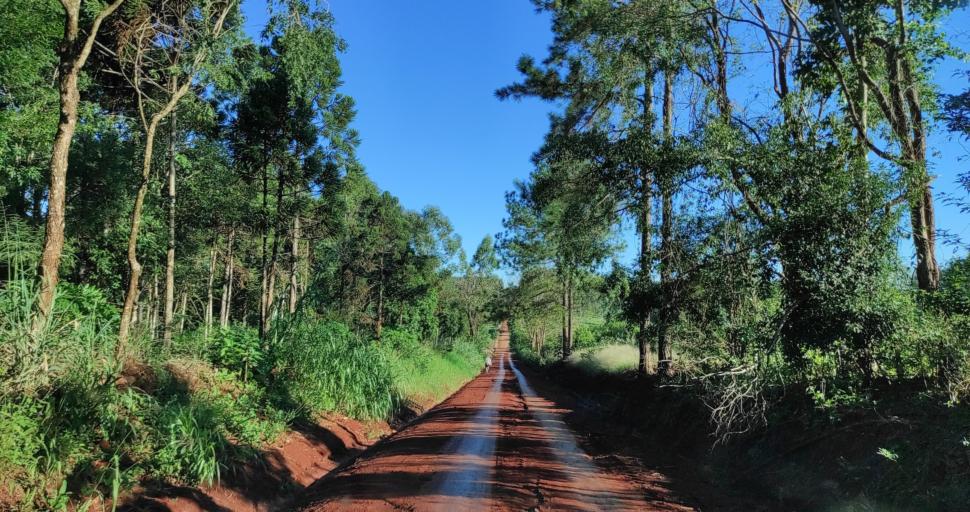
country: AR
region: Misiones
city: Puerto Rico
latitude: -26.8470
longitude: -55.0133
